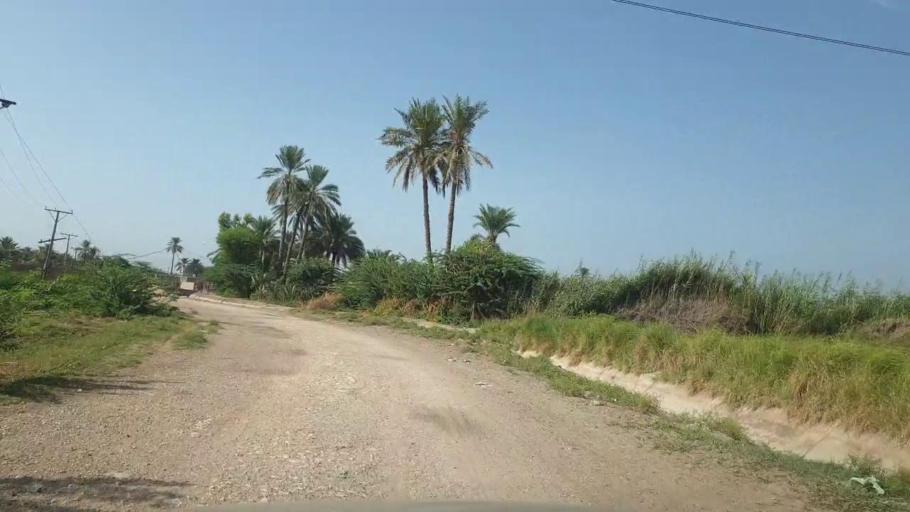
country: PK
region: Sindh
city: Rohri
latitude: 27.6615
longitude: 68.8836
